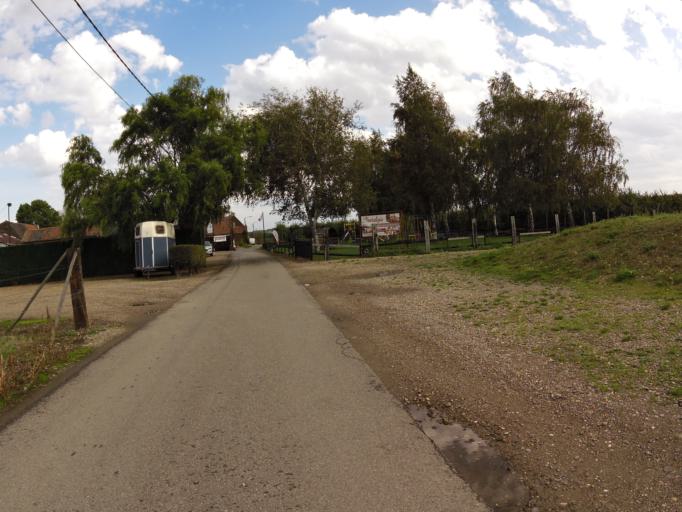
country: NL
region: Limburg
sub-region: Gemeente Meerssen
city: Meerssen
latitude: 50.9099
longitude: 5.7150
